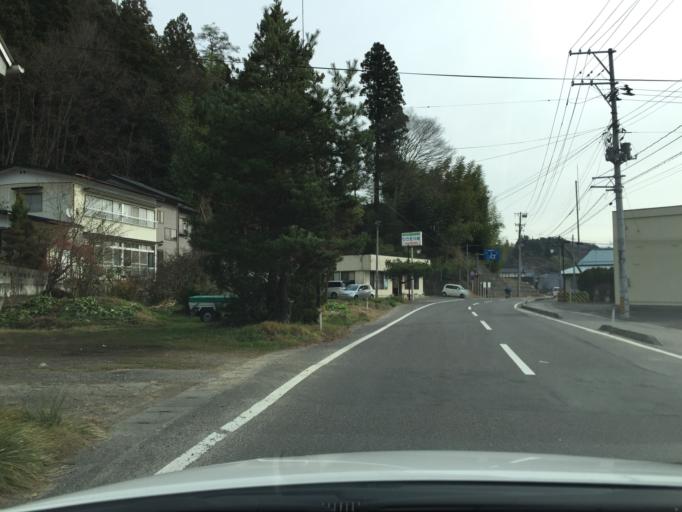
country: JP
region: Fukushima
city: Ishikawa
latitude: 37.2186
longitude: 140.5699
